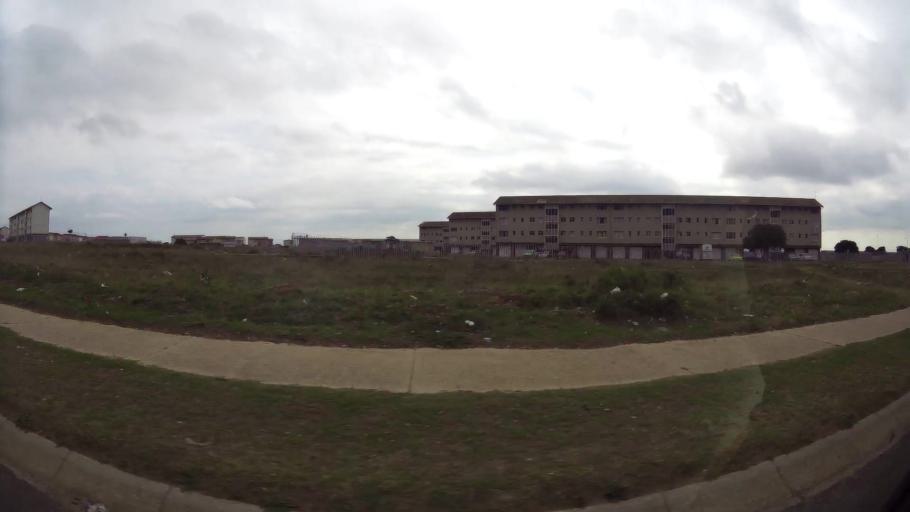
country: ZA
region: Eastern Cape
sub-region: Nelson Mandela Bay Metropolitan Municipality
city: Port Elizabeth
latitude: -33.8955
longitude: 25.5619
